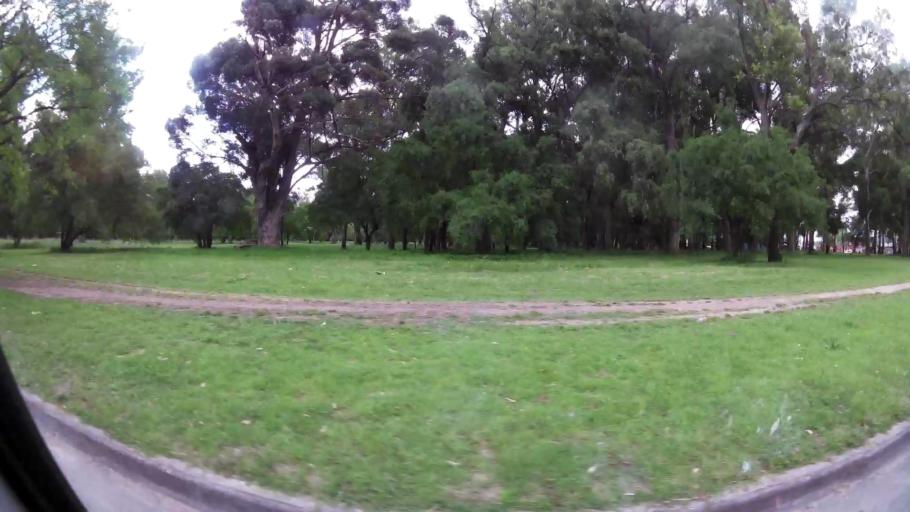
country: AR
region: Buenos Aires
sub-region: Partido de La Plata
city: La Plata
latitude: -34.9082
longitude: -57.9277
